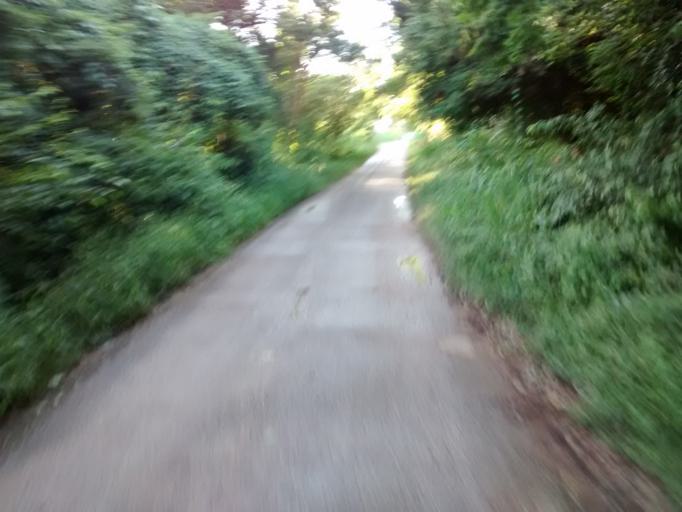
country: MX
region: Yucatan
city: Valladolid
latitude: 20.7274
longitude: -88.2322
